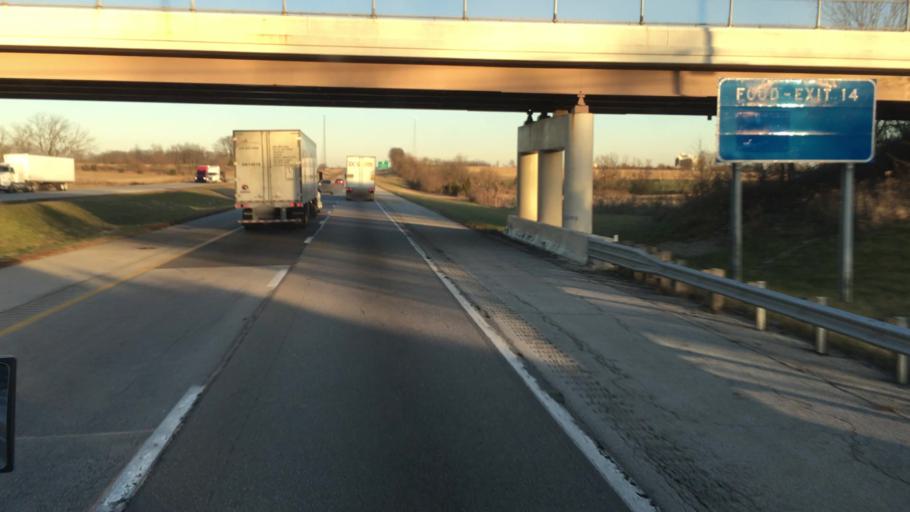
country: US
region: Ohio
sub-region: Preble County
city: Lewisburg
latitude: 39.8367
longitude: -84.5592
